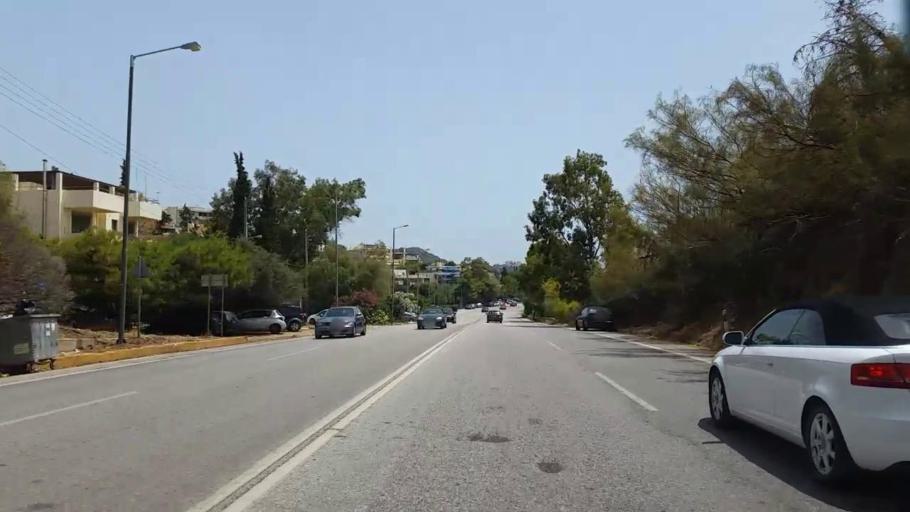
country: GR
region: Attica
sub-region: Nomarchia Anatolikis Attikis
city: Saronida
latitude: 37.7442
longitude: 23.9039
